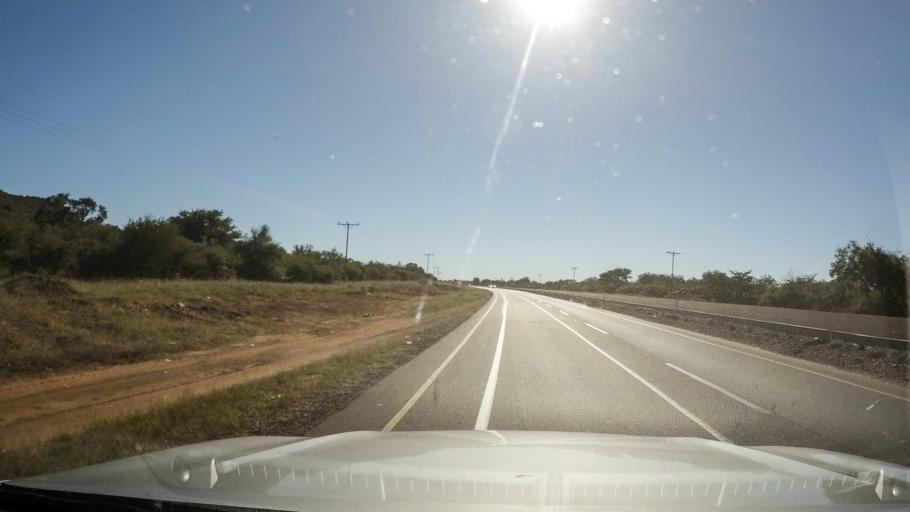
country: BW
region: South East
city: Gaborone
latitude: -24.7220
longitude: 25.8576
